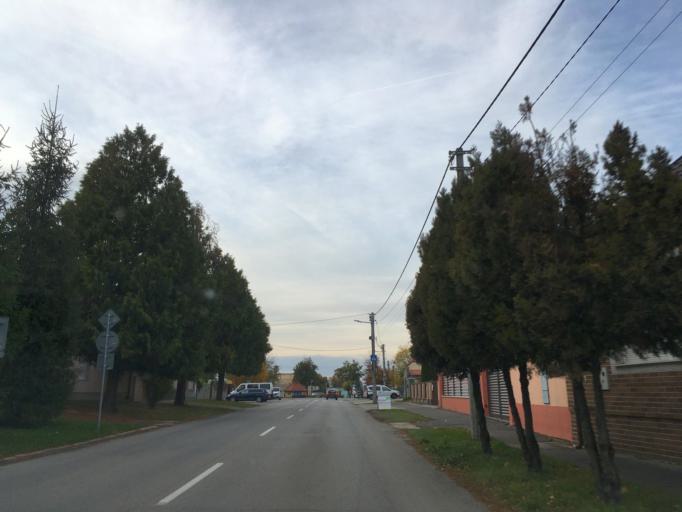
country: SK
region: Trnavsky
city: Samorin
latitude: 48.0981
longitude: 17.3558
